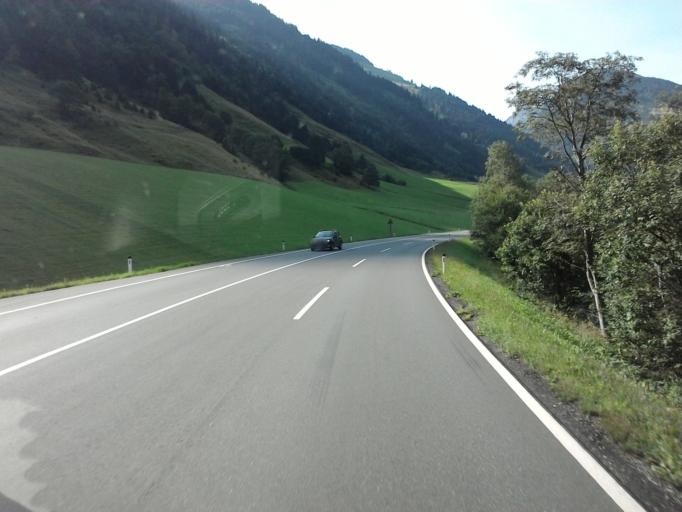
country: AT
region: Salzburg
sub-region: Politischer Bezirk Zell am See
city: Mittersill
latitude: 47.2443
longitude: 12.4908
